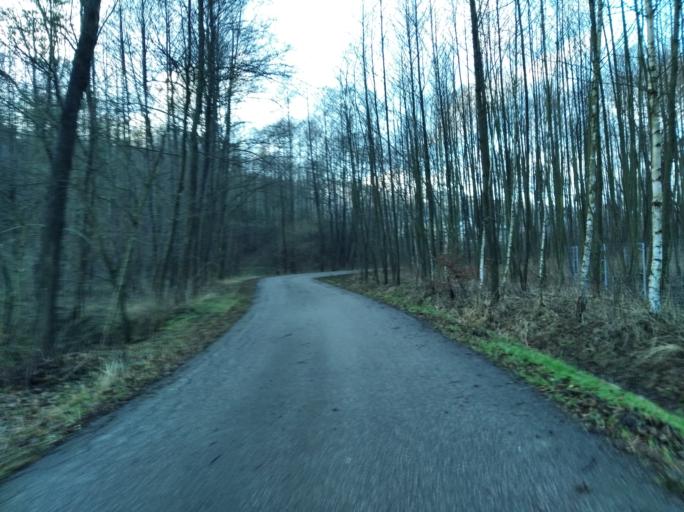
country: PL
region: Subcarpathian Voivodeship
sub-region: Powiat strzyzowski
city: Czudec
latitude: 49.9498
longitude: 21.7974
